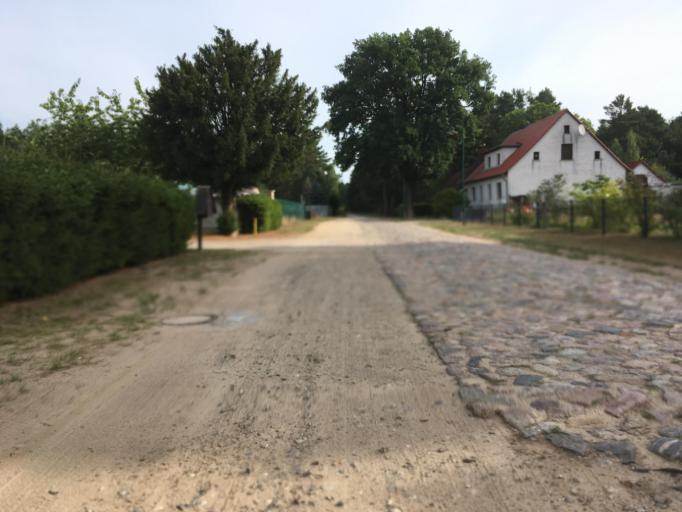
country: DE
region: Brandenburg
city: Templin
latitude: 52.9948
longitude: 13.5261
